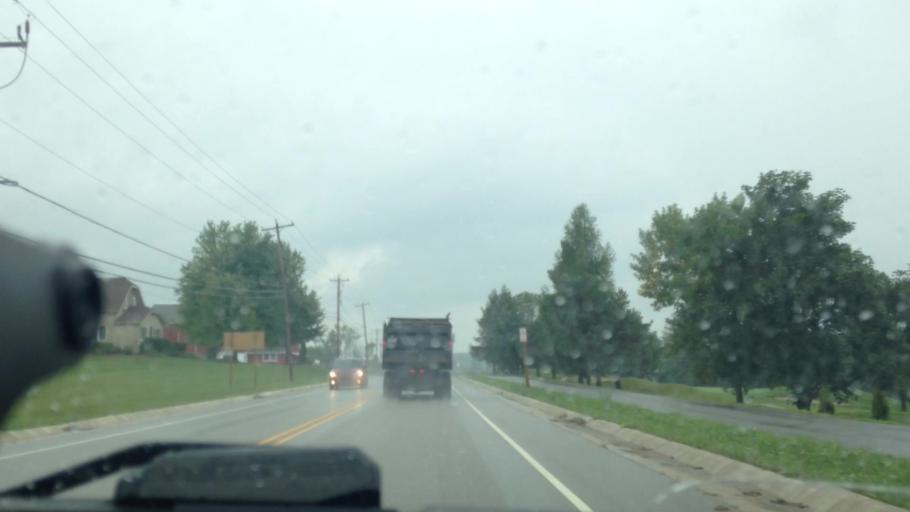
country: US
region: Wisconsin
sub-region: Washington County
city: Richfield
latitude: 43.2417
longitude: -88.1887
